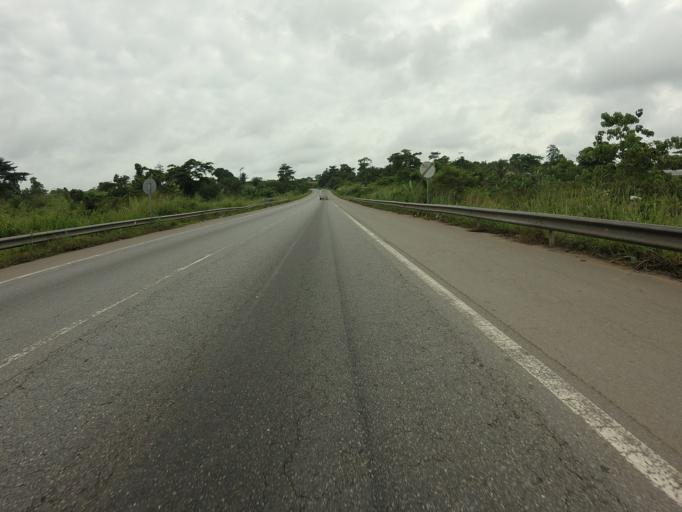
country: GH
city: Bechem
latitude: 7.1063
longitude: -1.7227
